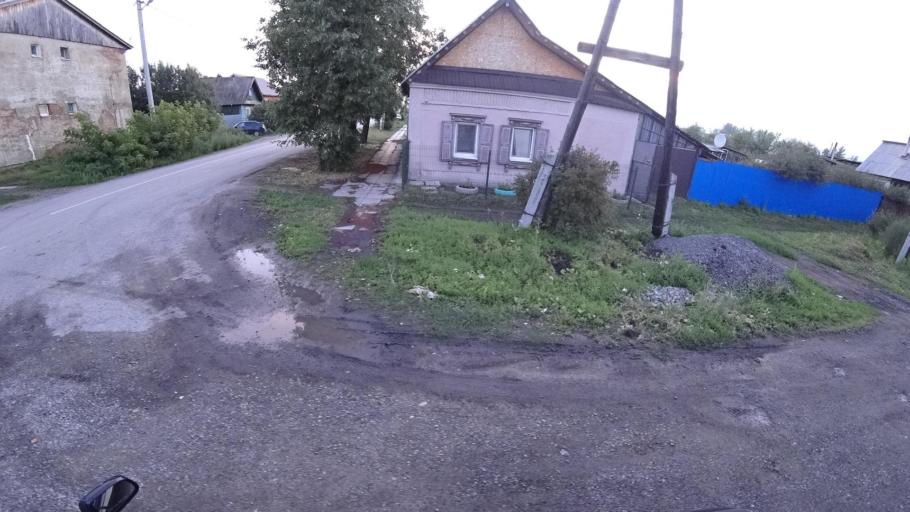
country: RU
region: Sverdlovsk
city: Kamyshlov
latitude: 56.8503
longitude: 62.7301
